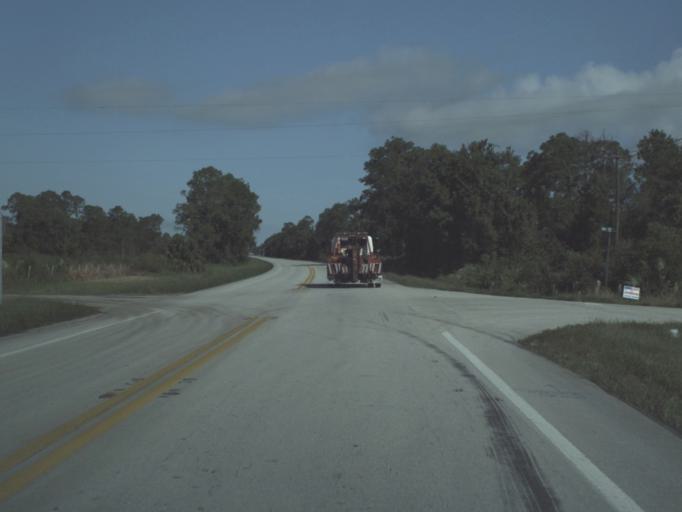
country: US
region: Florida
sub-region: Indian River County
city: Fellsmere
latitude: 27.5796
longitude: -80.8350
